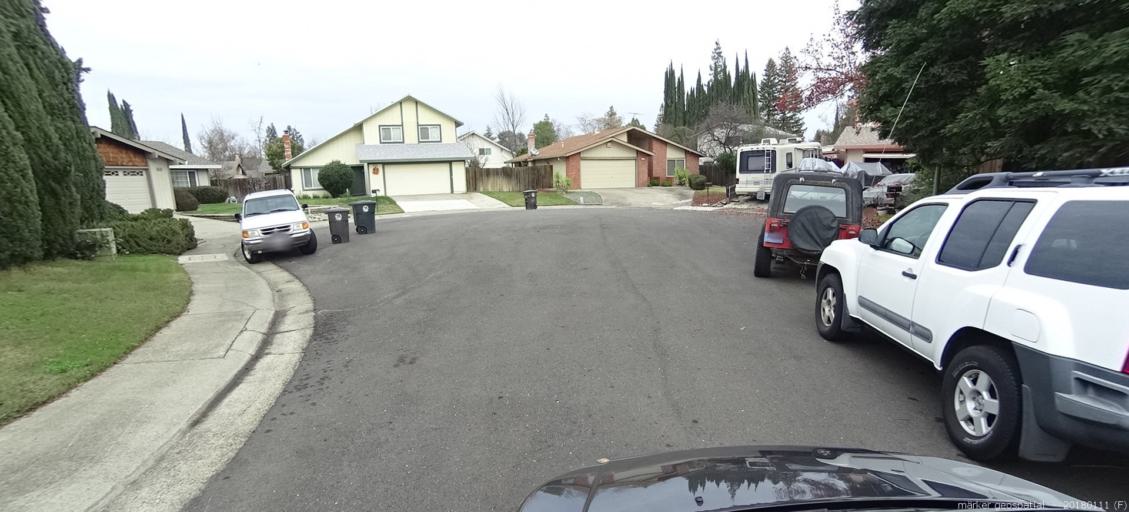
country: US
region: California
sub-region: Sacramento County
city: Fair Oaks
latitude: 38.6198
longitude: -121.2779
